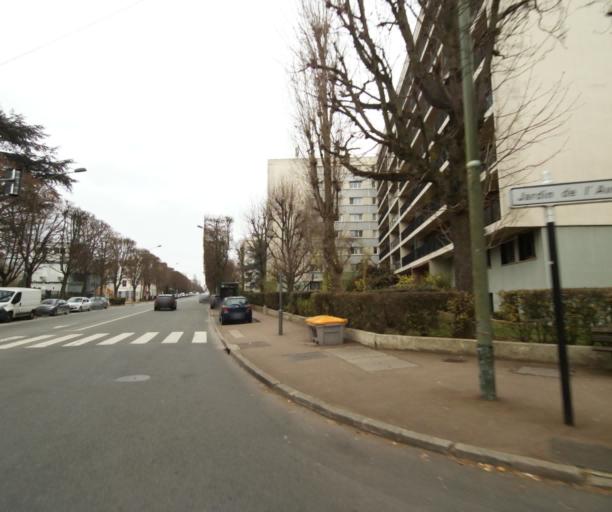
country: FR
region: Ile-de-France
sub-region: Departement des Hauts-de-Seine
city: Saint-Cloud
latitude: 48.8568
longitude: 2.2112
